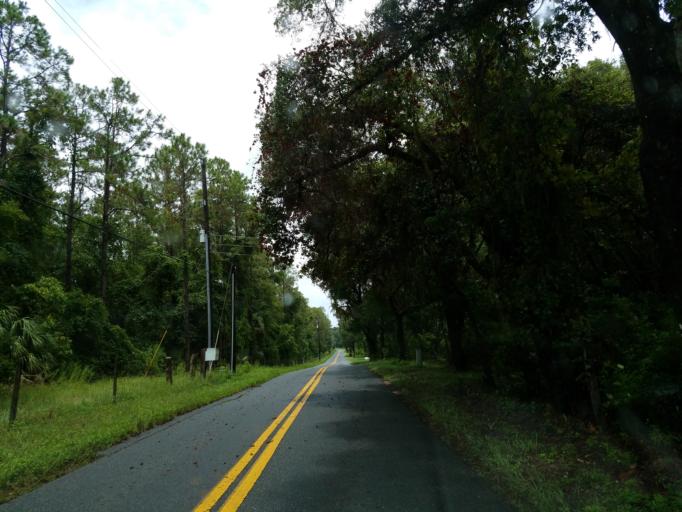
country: US
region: Florida
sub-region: Citrus County
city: Inverness Highlands South
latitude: 28.8025
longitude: -82.2952
